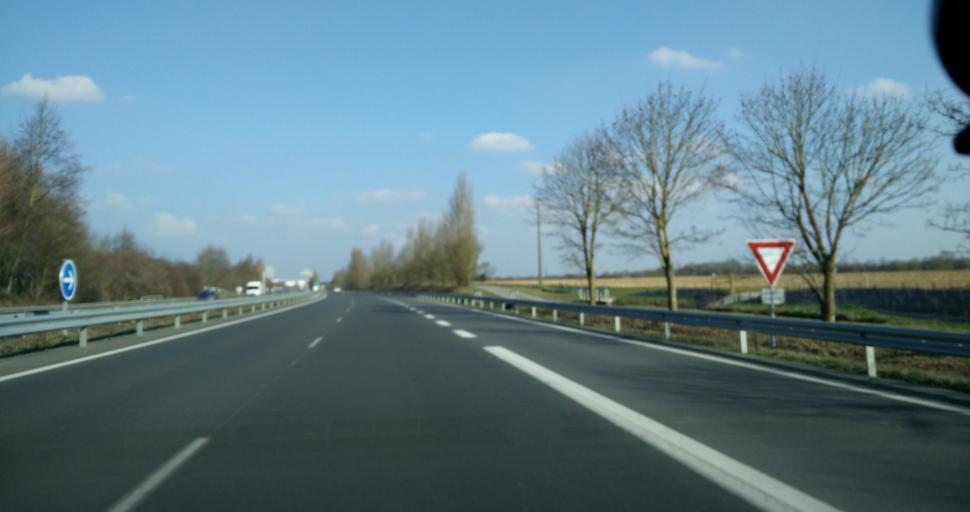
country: FR
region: Poitou-Charentes
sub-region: Departement de la Charente-Maritime
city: Sainte-Soulle
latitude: 46.2015
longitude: -1.0262
